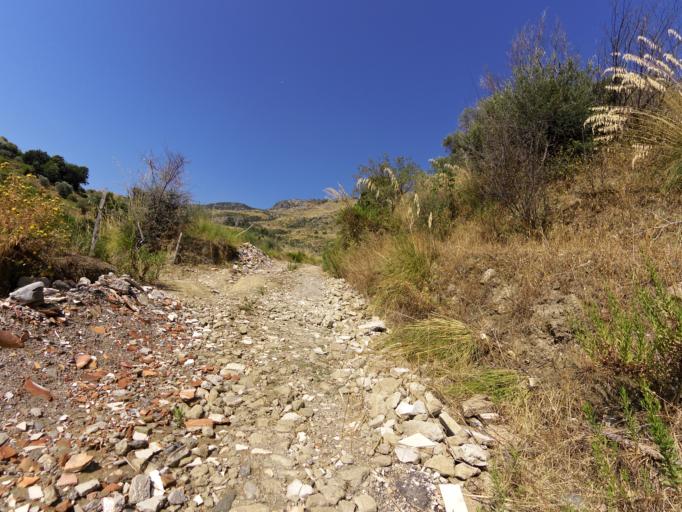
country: IT
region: Calabria
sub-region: Provincia di Reggio Calabria
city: Pazzano
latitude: 38.4632
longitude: 16.4557
